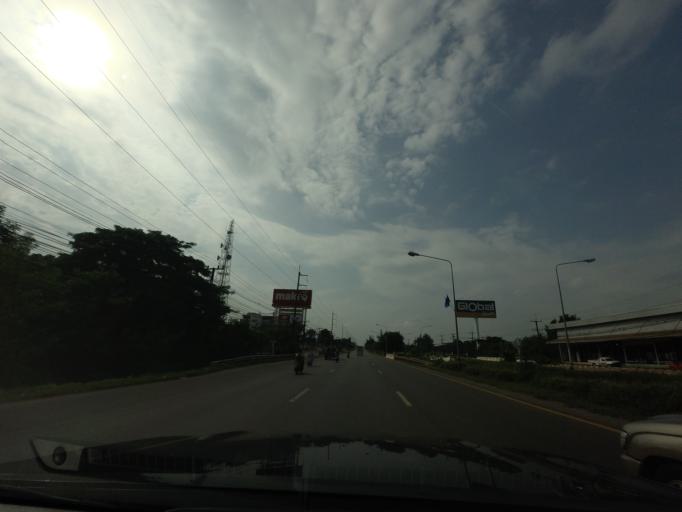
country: TH
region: Nong Khai
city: Nong Khai
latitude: 17.8358
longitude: 102.7543
